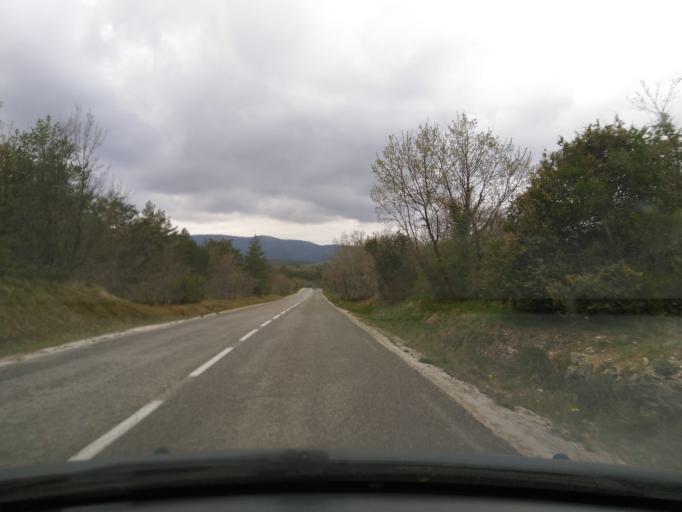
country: FR
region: Languedoc-Roussillon
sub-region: Departement du Gard
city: Barjac
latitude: 44.3591
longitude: 4.3729
